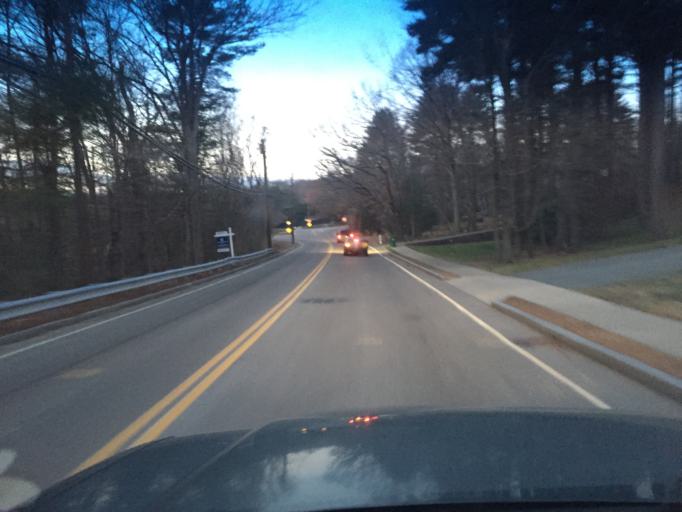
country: US
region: Massachusetts
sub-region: Norfolk County
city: Westwood
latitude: 42.2074
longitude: -71.2226
